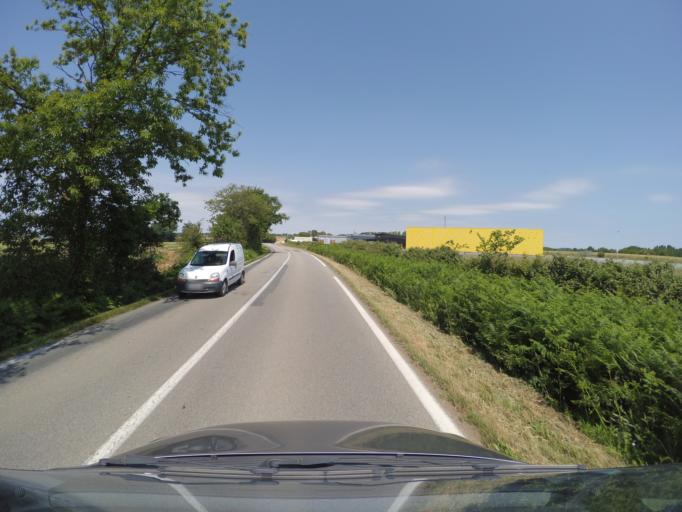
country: FR
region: Pays de la Loire
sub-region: Departement de la Vendee
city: La Flocelliere
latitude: 46.8143
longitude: -0.8651
